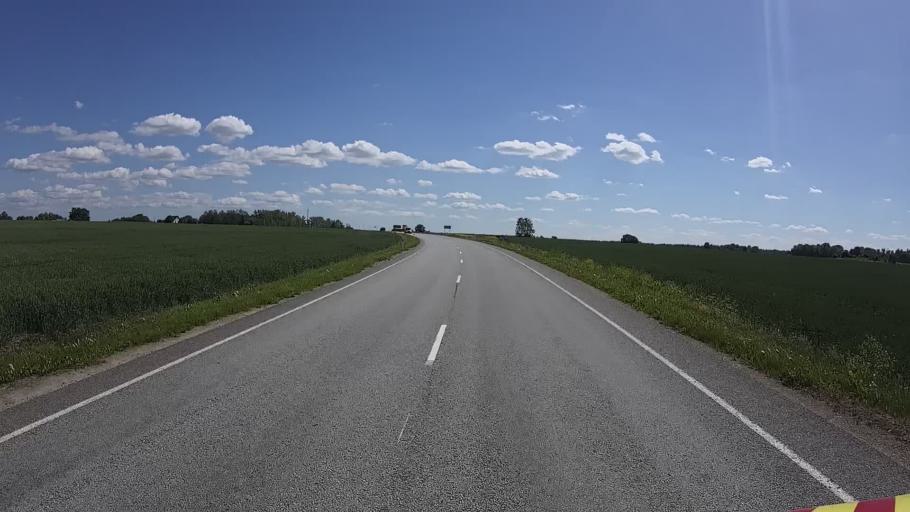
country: EE
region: Ida-Virumaa
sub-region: Johvi vald
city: Johvi
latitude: 59.3736
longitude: 27.3490
